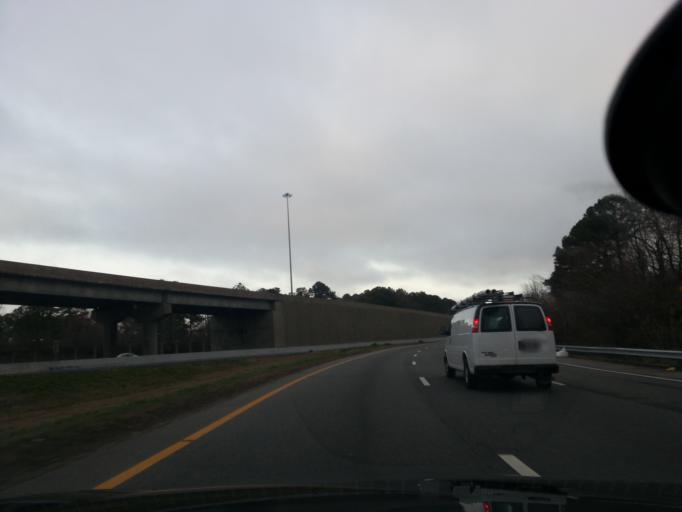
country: US
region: Virginia
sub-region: City of Chesapeake
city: Chesapeake
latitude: 36.8483
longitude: -76.1955
